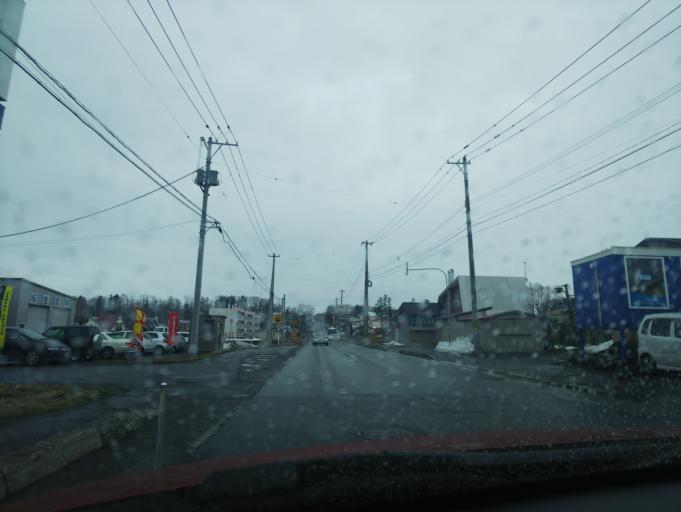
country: JP
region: Hokkaido
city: Nayoro
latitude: 44.3363
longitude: 142.4644
